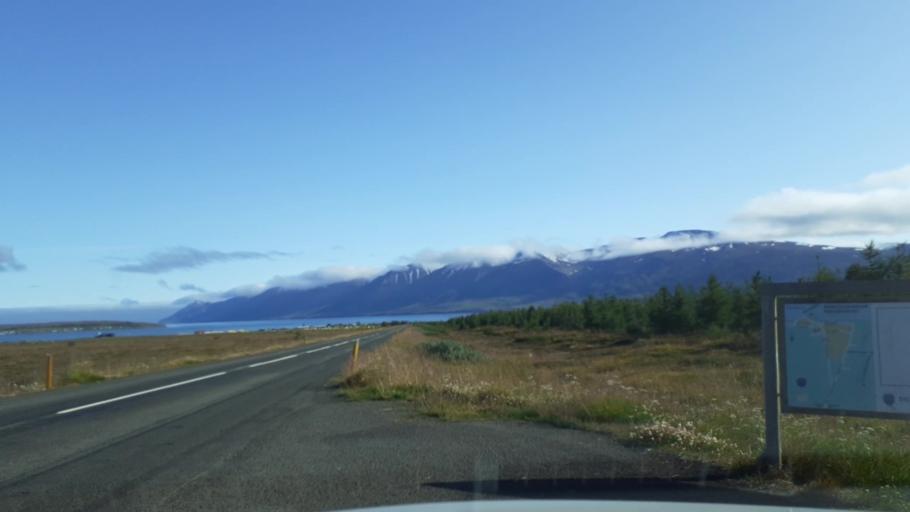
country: IS
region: Northeast
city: Dalvik
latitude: 65.9293
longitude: -18.3634
